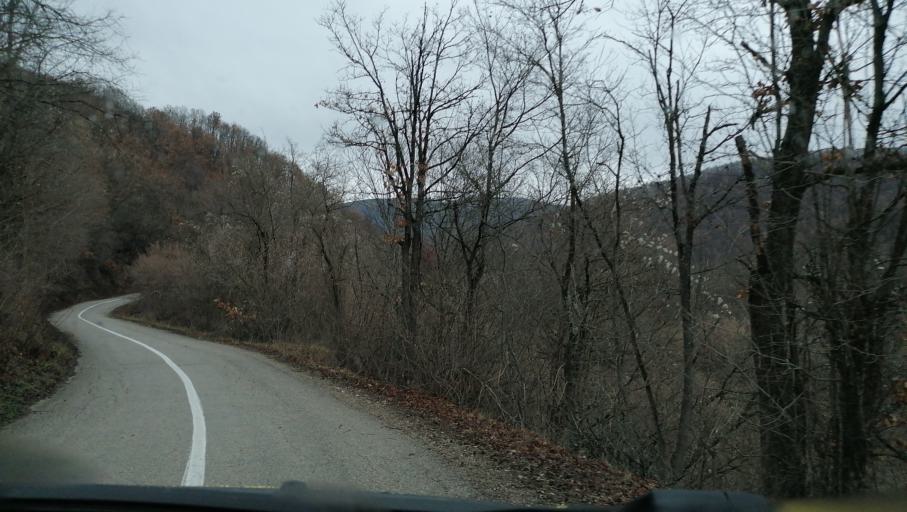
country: RS
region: Central Serbia
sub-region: Pirotski Okrug
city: Dimitrovgrad
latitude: 42.9633
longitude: 22.7826
